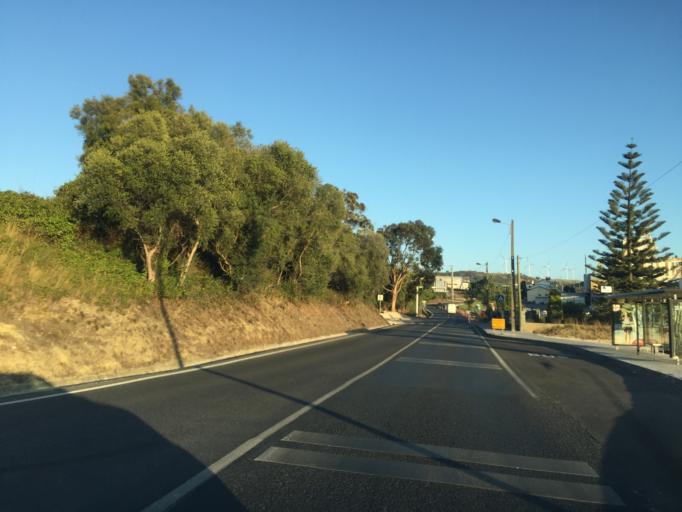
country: PT
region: Lisbon
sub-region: Torres Vedras
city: Torres Vedras
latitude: 39.0751
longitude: -9.2513
